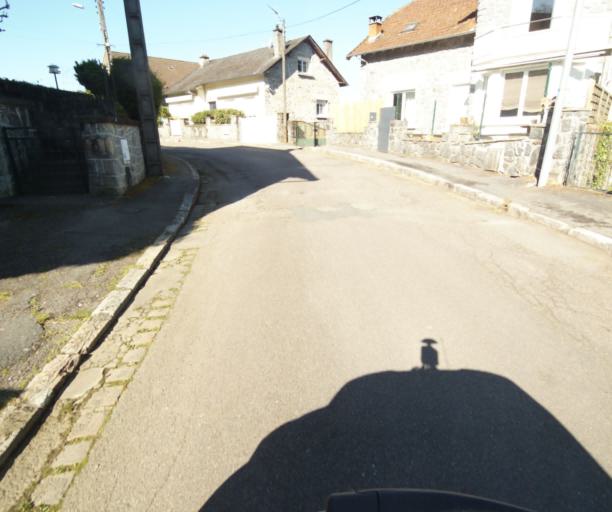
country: FR
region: Limousin
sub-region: Departement de la Correze
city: Tulle
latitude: 45.2709
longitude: 1.7784
